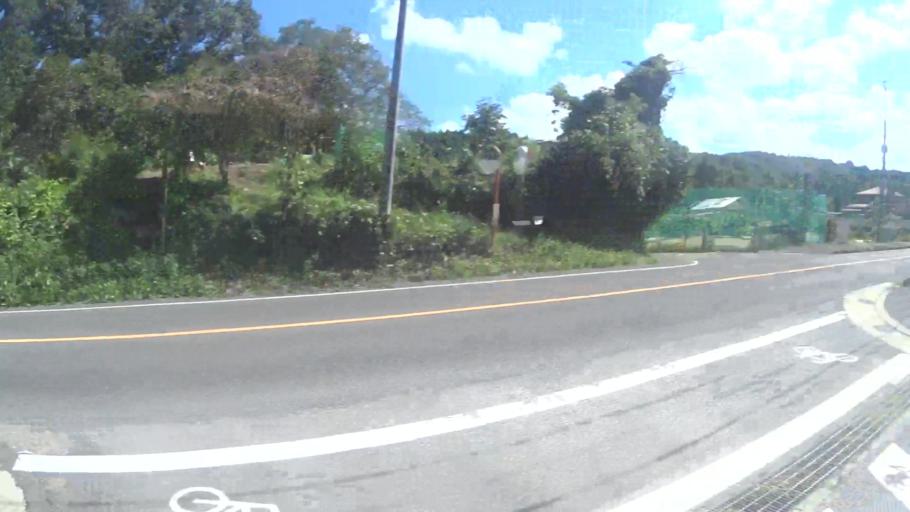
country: JP
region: Nara
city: Nara-shi
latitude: 34.7593
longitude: 135.8719
